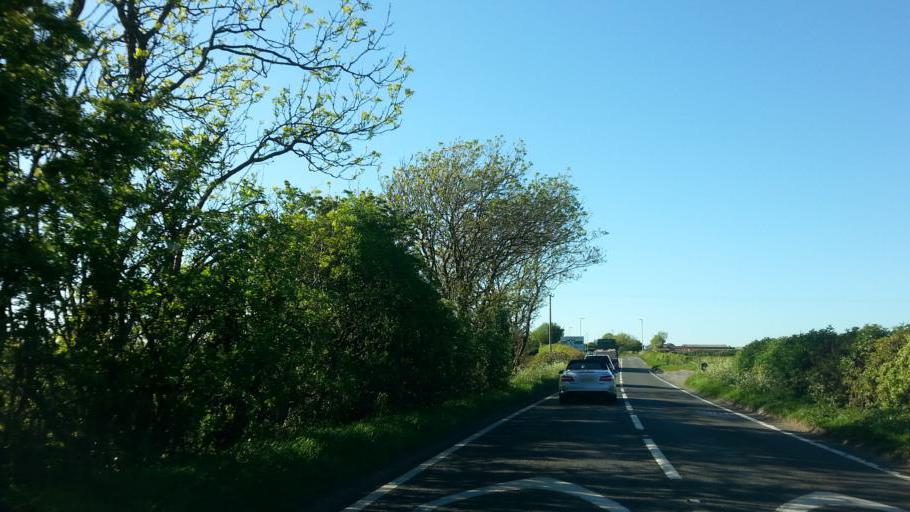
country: GB
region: England
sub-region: Somerset
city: Shepton Mallet
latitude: 51.1681
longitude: -2.5333
